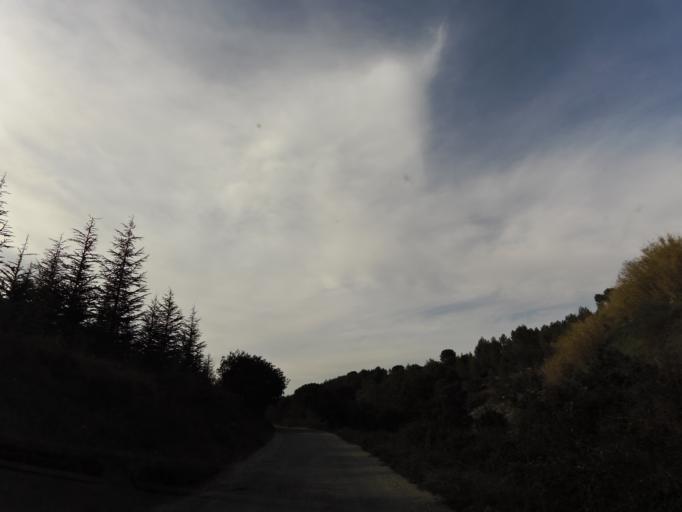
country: FR
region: Languedoc-Roussillon
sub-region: Departement du Gard
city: Congenies
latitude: 43.7867
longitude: 4.1682
